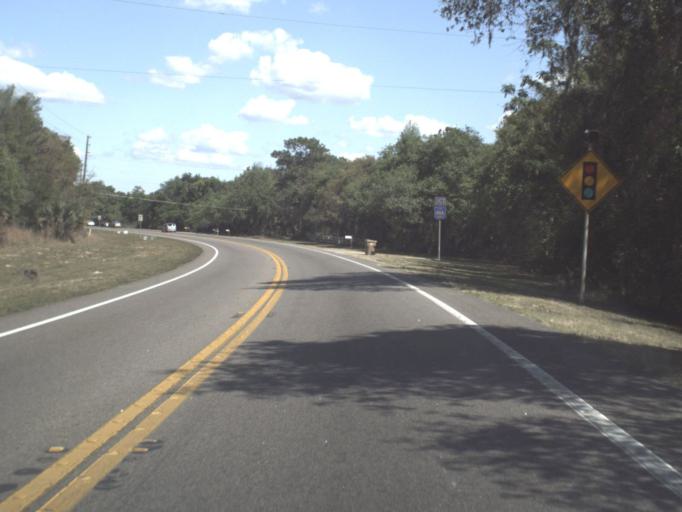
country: US
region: Florida
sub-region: Lake County
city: Mount Plymouth
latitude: 28.8116
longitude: -81.4651
